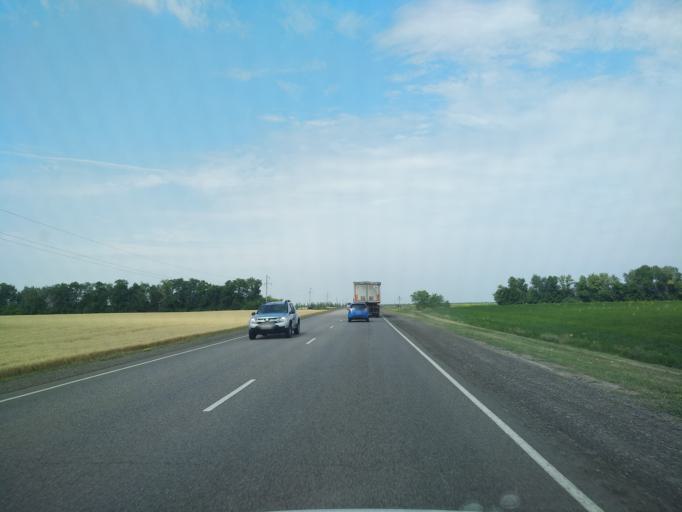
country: RU
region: Voronezj
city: Orlovo
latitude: 51.6834
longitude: 39.5577
